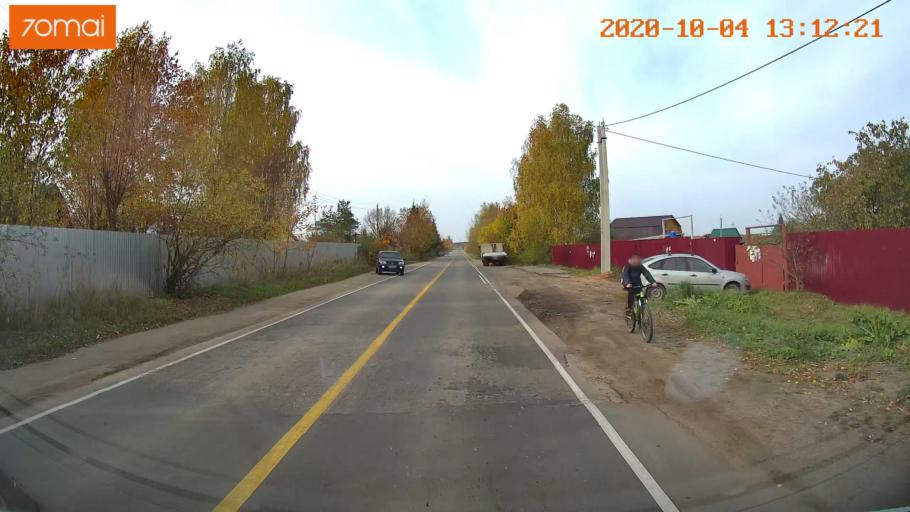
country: RU
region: Ivanovo
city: Bogorodskoye
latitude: 57.0837
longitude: 40.9282
